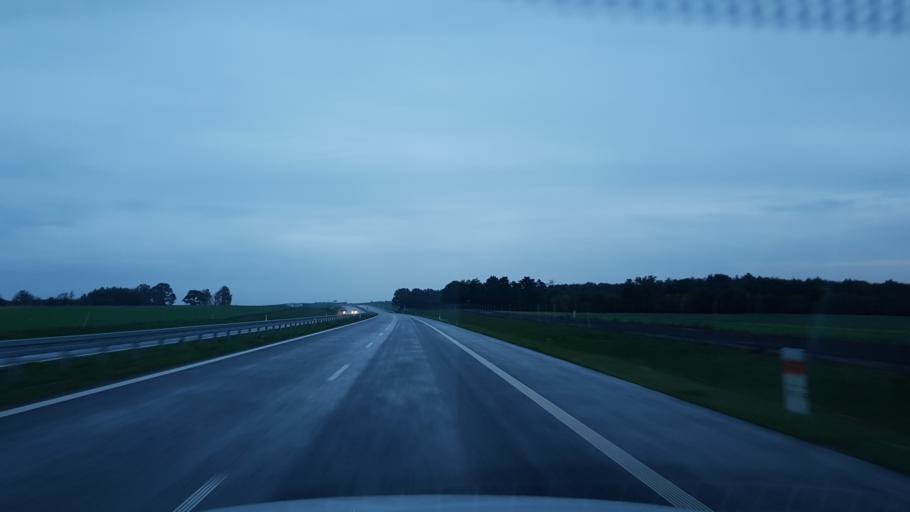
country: PL
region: West Pomeranian Voivodeship
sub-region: Powiat gryficki
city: Brojce
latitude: 53.9615
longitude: 15.4205
